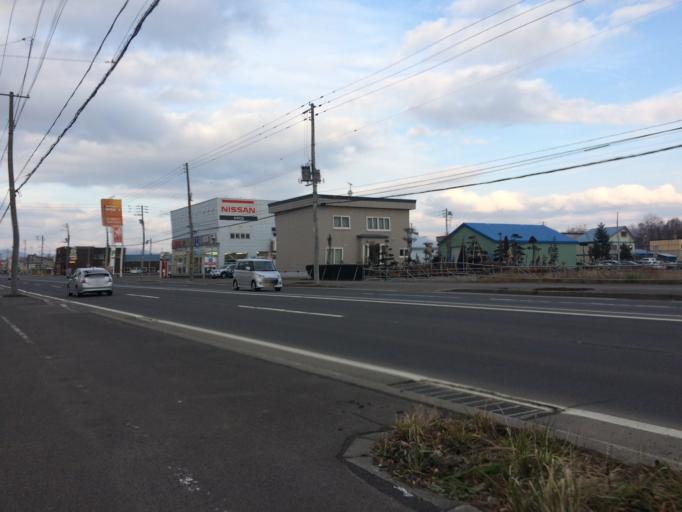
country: JP
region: Hokkaido
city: Niseko Town
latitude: 42.8919
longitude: 140.7516
